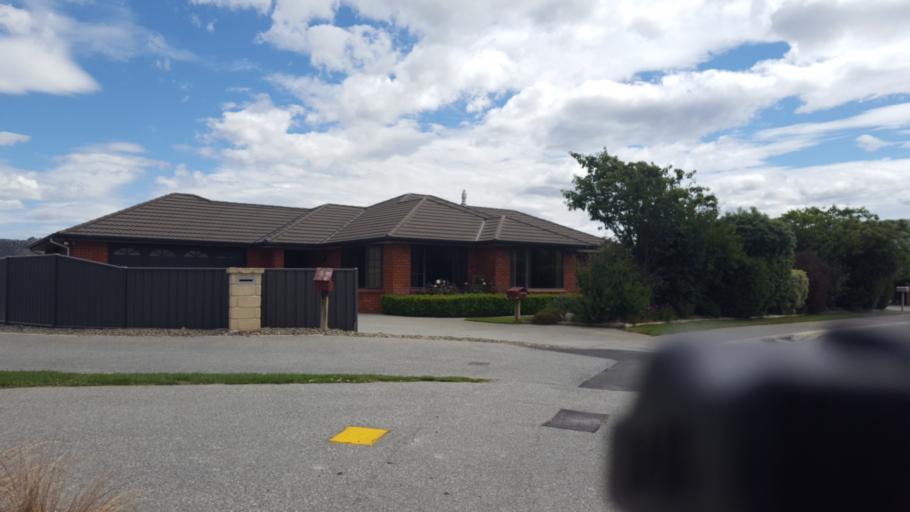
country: NZ
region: Otago
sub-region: Queenstown-Lakes District
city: Wanaka
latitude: -45.0390
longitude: 169.2167
